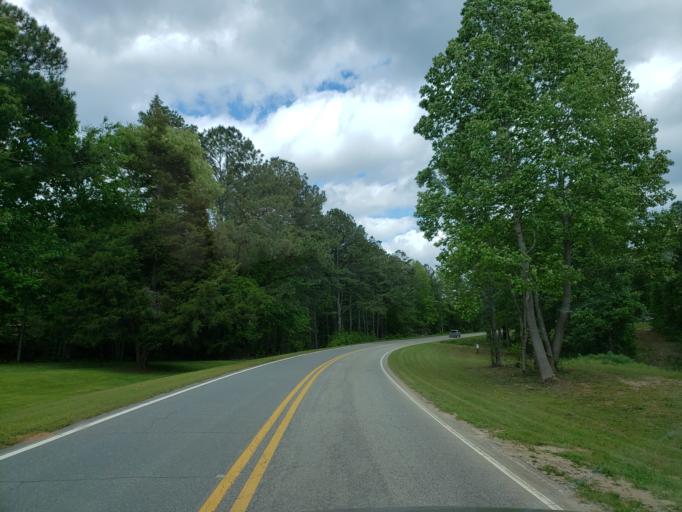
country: US
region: Georgia
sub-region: Haralson County
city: Tallapoosa
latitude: 33.6977
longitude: -85.3389
